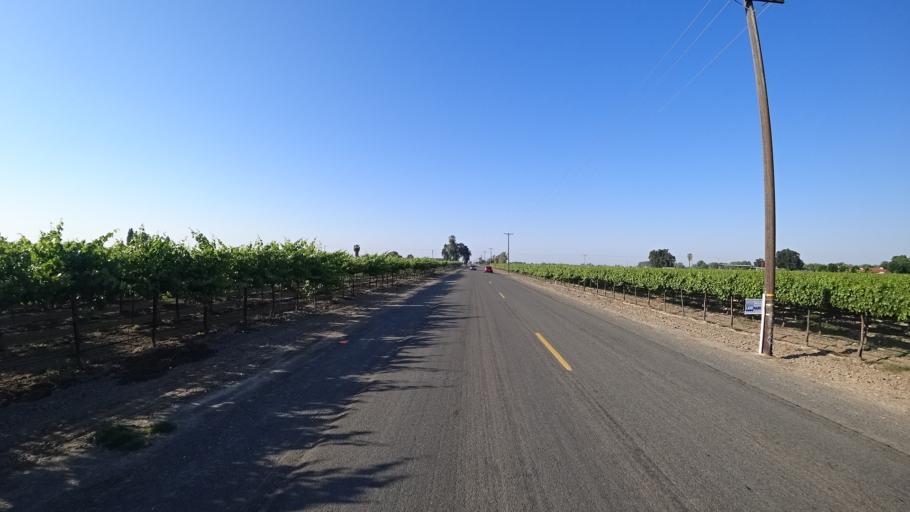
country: US
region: California
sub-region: Kings County
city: Lemoore
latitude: 36.2572
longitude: -119.7446
